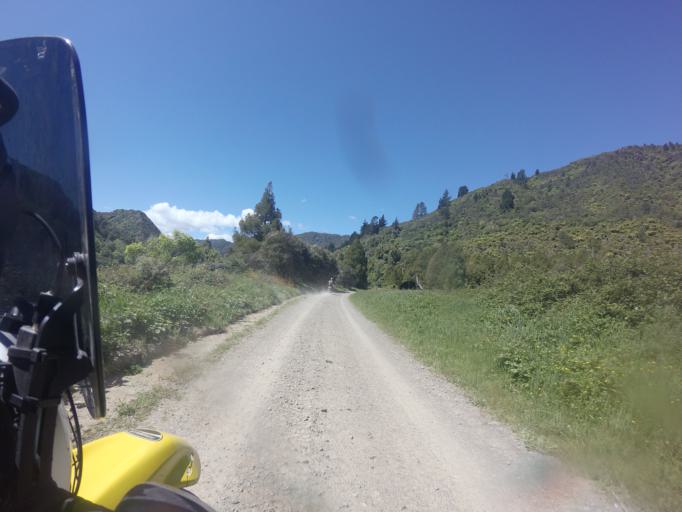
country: NZ
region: Bay of Plenty
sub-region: Opotiki District
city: Opotiki
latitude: -38.2978
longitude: 177.3353
